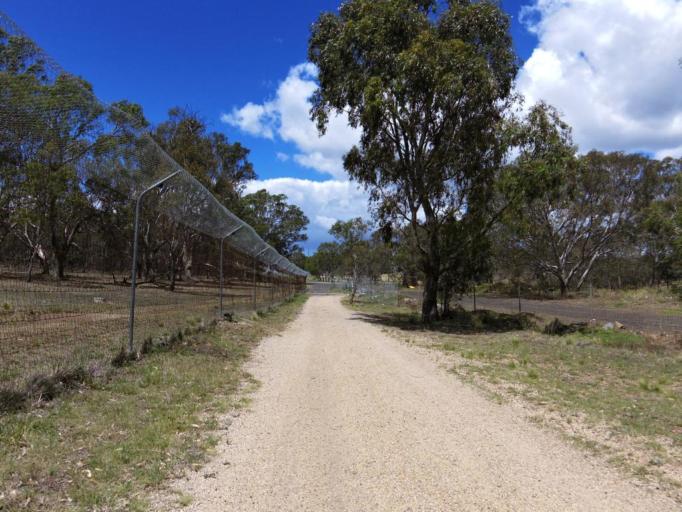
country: AU
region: Victoria
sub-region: Hume
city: Greenvale
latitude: -37.6598
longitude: 144.8586
